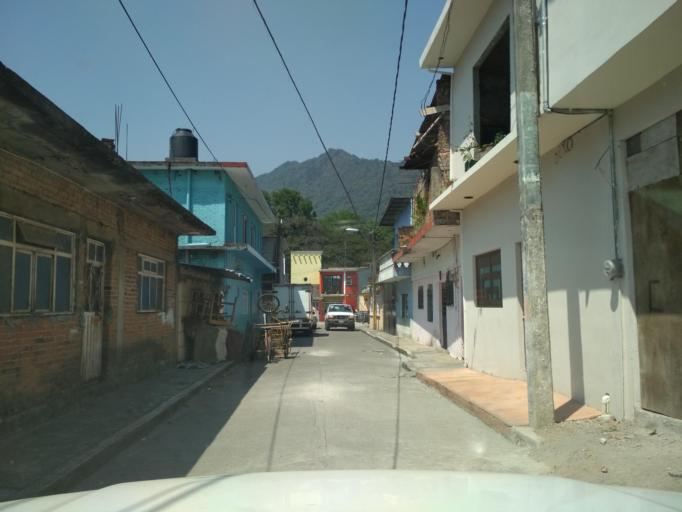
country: MX
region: Veracruz
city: Rio Blanco
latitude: 18.8435
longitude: -97.1251
